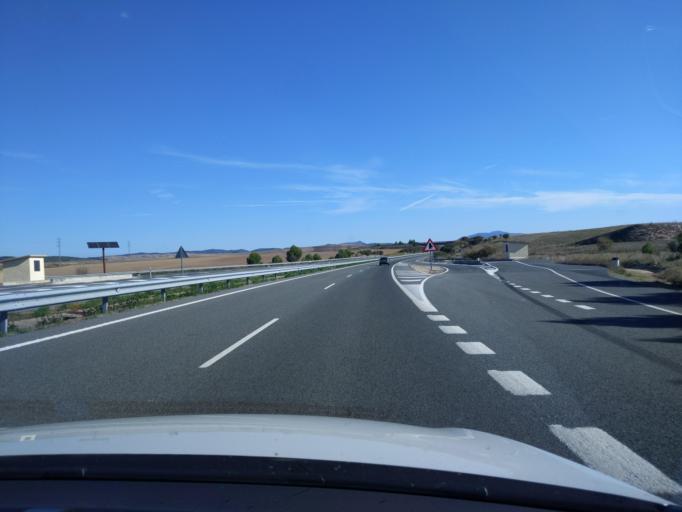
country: ES
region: Navarre
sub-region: Provincia de Navarra
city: Los Arcos
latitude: 42.5389
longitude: -2.2144
